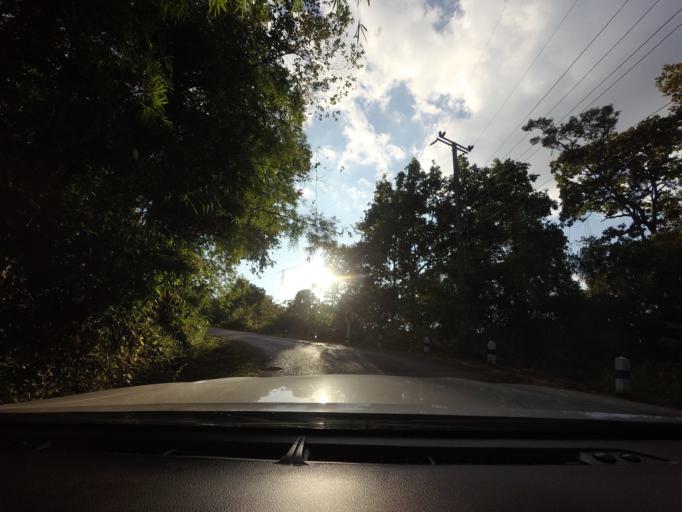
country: TH
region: Chiang Mai
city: Phrao
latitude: 19.5065
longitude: 99.1694
